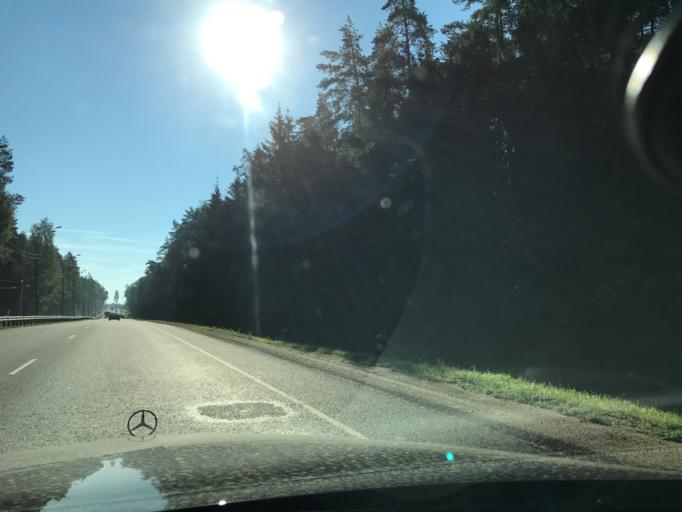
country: RU
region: Moskovskaya
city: Sverdlovskiy
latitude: 55.9280
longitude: 38.1858
